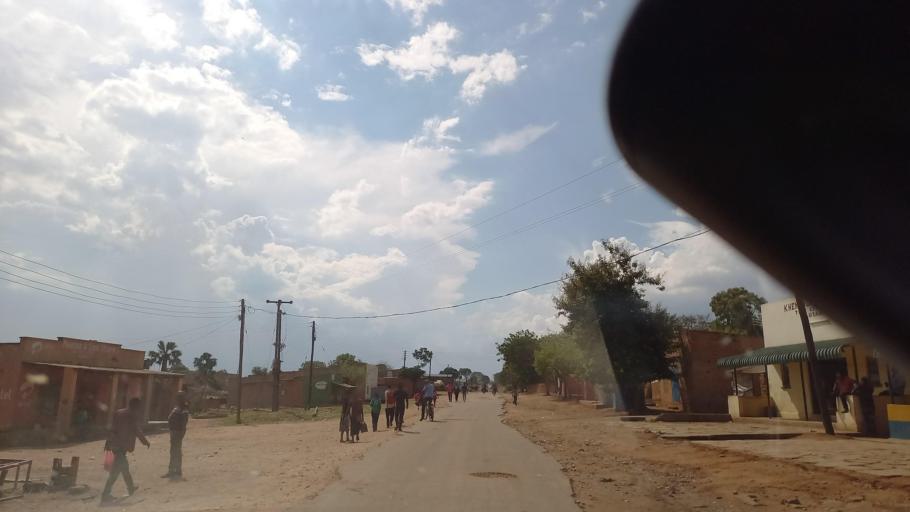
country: ZM
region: Lusaka
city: Kafue
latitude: -16.2280
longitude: 28.1408
